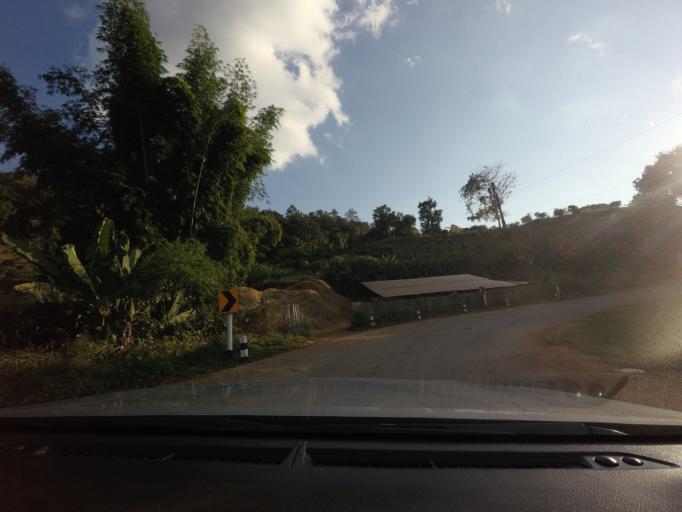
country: TH
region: Chiang Mai
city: Phrao
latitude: 19.4943
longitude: 99.1670
